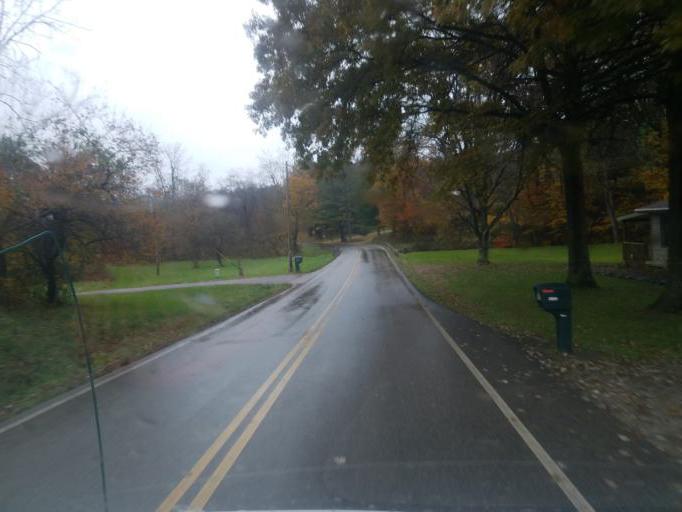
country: US
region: West Virginia
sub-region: Wood County
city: Blennerhassett
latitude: 39.3277
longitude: -81.6216
